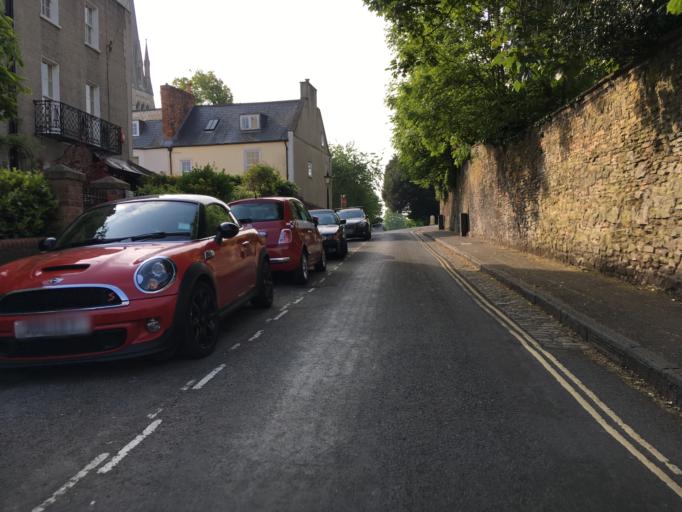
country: GB
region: England
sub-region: Bristol
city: Bristol
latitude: 51.4581
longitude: -2.6215
